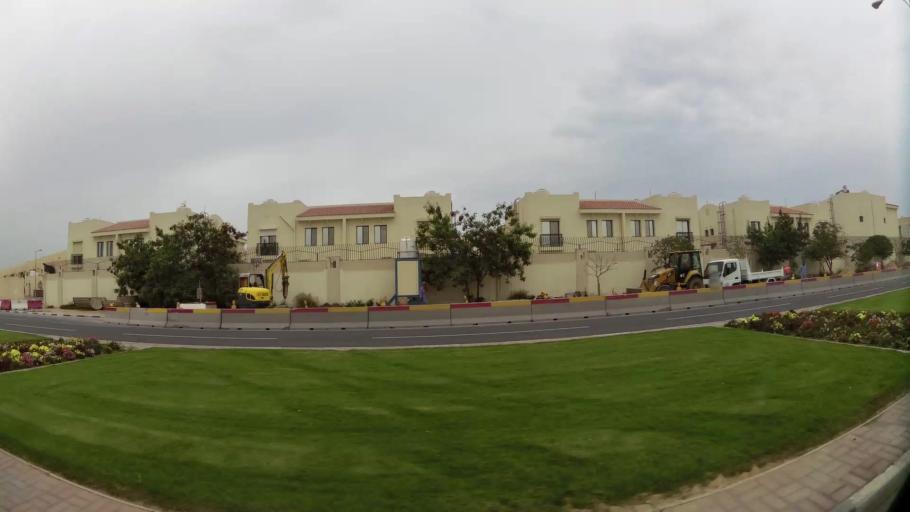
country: QA
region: Baladiyat ad Dawhah
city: Doha
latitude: 25.3278
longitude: 51.4843
